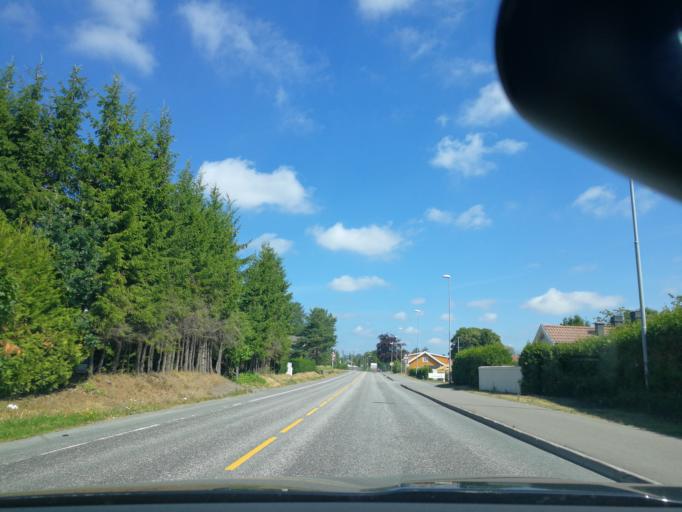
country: NO
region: Vestfold
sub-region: Sandefjord
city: Sandefjord
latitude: 59.1612
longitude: 10.2012
